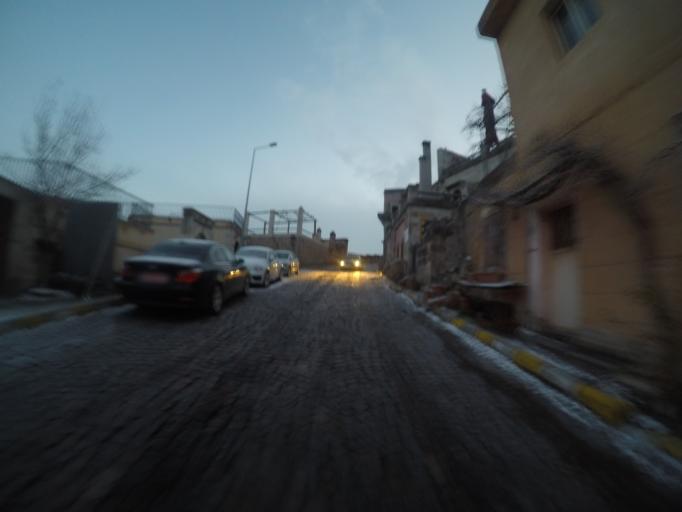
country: TR
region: Nevsehir
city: Goereme
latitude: 38.6305
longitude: 34.8070
